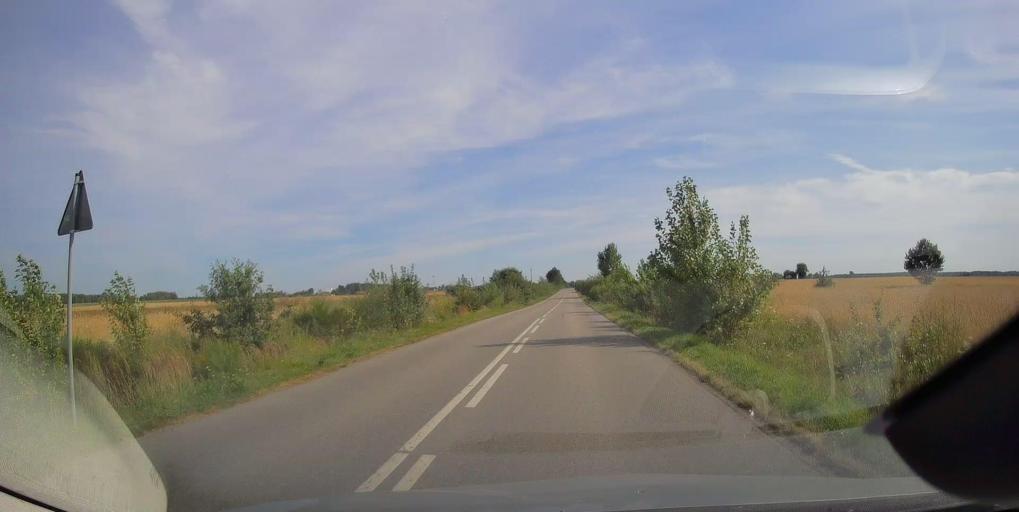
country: PL
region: Lodz Voivodeship
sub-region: Powiat opoczynski
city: Mniszkow
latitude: 51.3851
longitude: 20.0347
